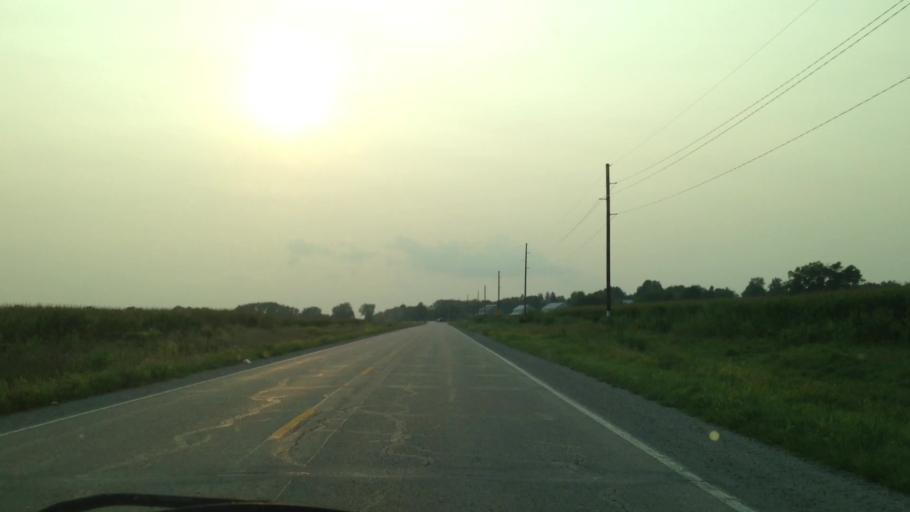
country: US
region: Iowa
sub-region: Iowa County
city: Marengo
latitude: 41.8041
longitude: -91.9544
